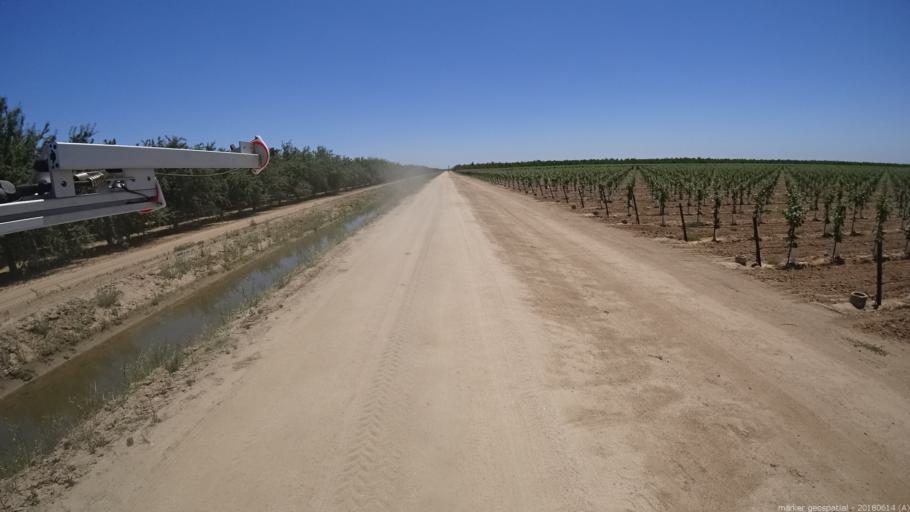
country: US
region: California
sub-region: Madera County
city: Fairmead
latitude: 37.0324
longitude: -120.2295
